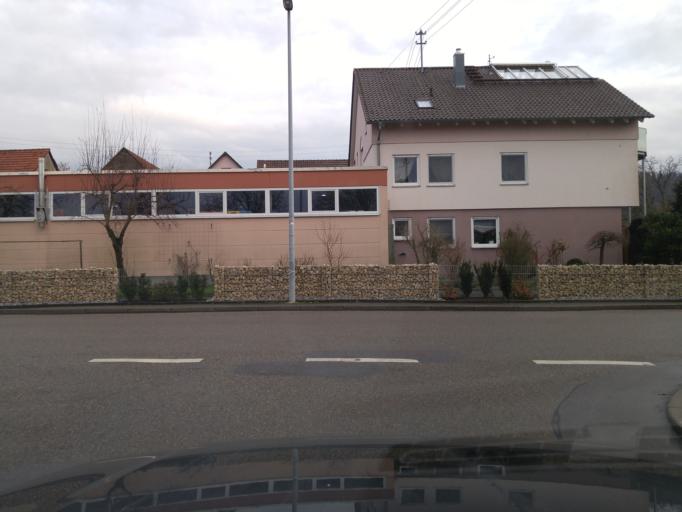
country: DE
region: Baden-Wuerttemberg
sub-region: Regierungsbezirk Stuttgart
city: Neuenstein
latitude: 49.1892
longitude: 9.5712
